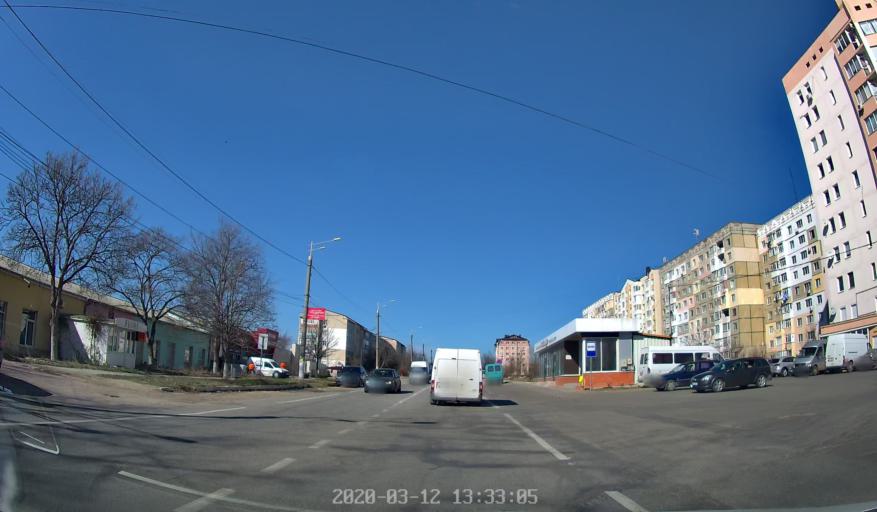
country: MD
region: Laloveni
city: Ialoveni
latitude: 46.9547
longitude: 28.7698
